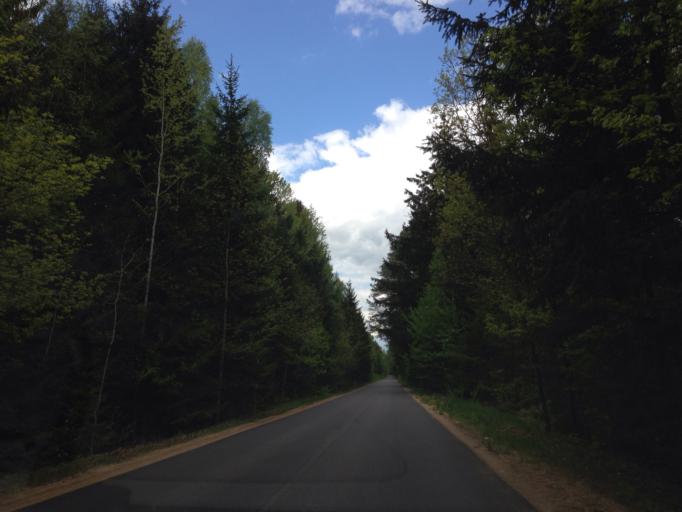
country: PL
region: Podlasie
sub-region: Powiat grajewski
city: Radzilow
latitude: 53.3349
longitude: 22.5992
